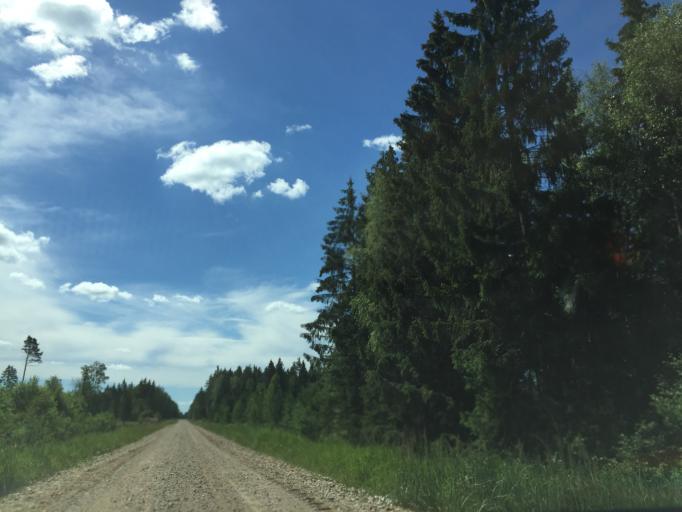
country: LV
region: Ventspils Rajons
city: Piltene
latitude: 57.2711
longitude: 21.8341
